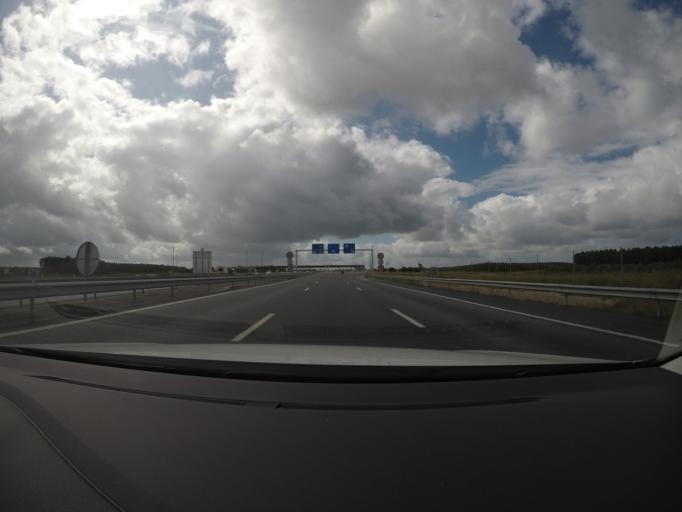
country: FR
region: Aquitaine
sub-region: Departement des Landes
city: Pissos
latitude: 44.3503
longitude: -0.8582
